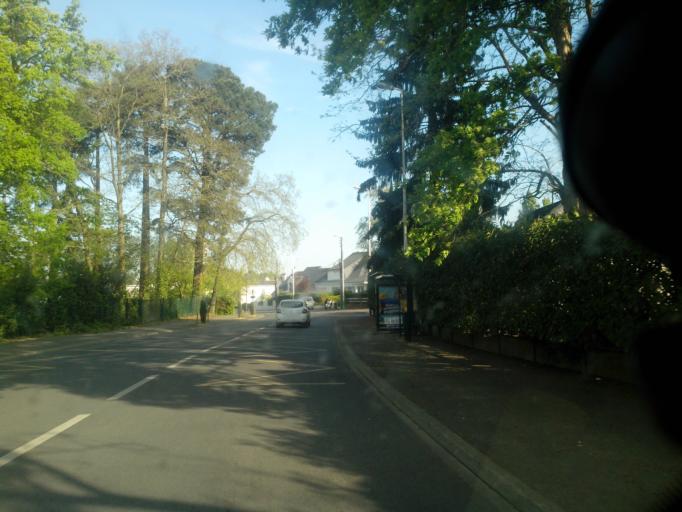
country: FR
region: Pays de la Loire
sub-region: Departement de la Loire-Atlantique
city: Orvault
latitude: 47.2383
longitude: -1.5983
